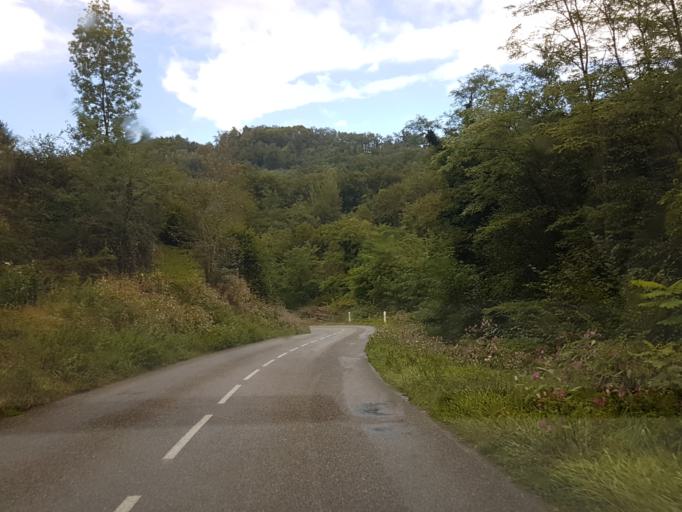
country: FR
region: Midi-Pyrenees
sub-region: Departement de l'Ariege
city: Saint-Girons
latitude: 42.9005
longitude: 1.2295
